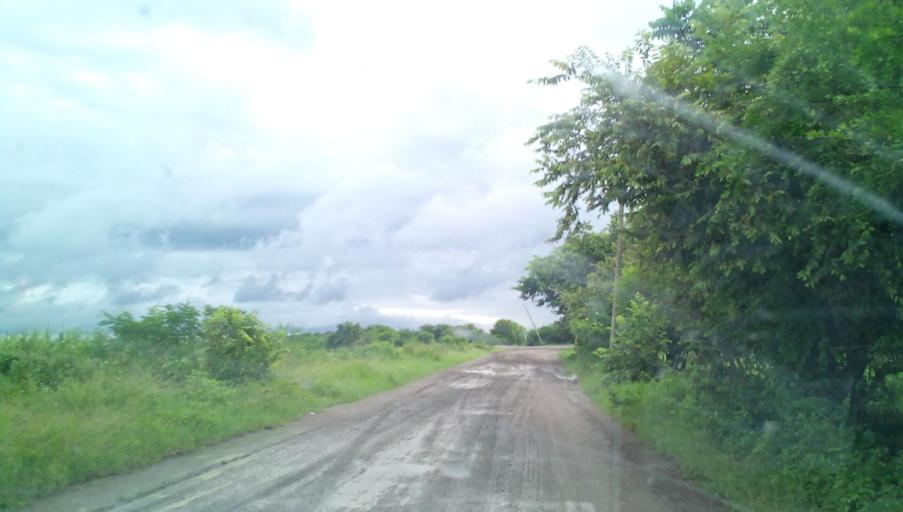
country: MX
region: Veracruz
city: Panuco
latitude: 21.8443
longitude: -98.1317
